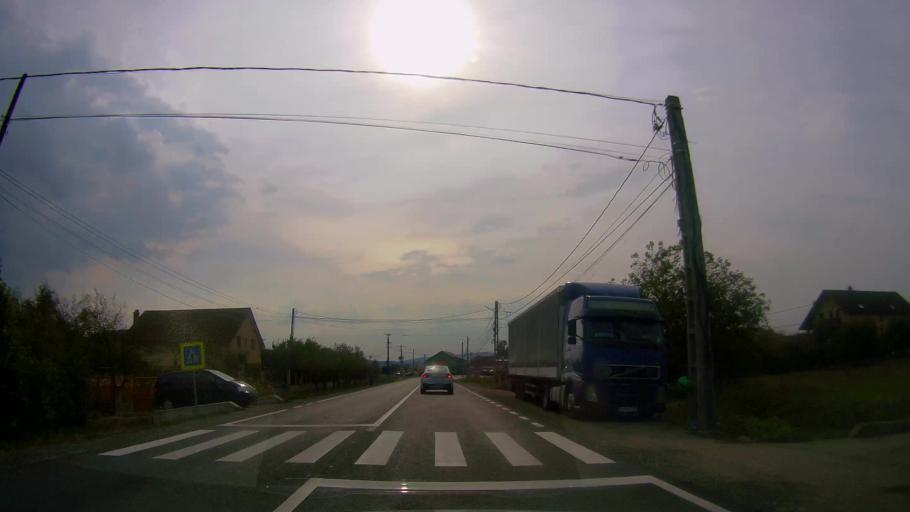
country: RO
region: Salaj
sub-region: Comuna Hereclean
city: Hereclean
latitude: 47.2427
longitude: 22.9916
